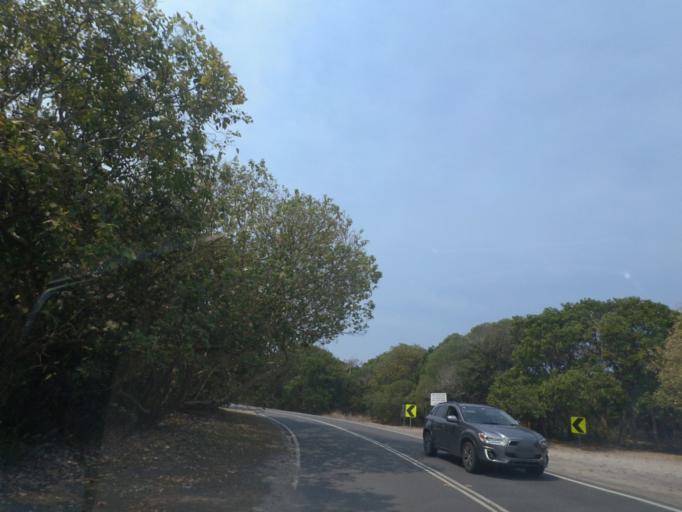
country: AU
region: New South Wales
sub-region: Tweed
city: Pottsville Beach
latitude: -28.4569
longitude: 153.5531
